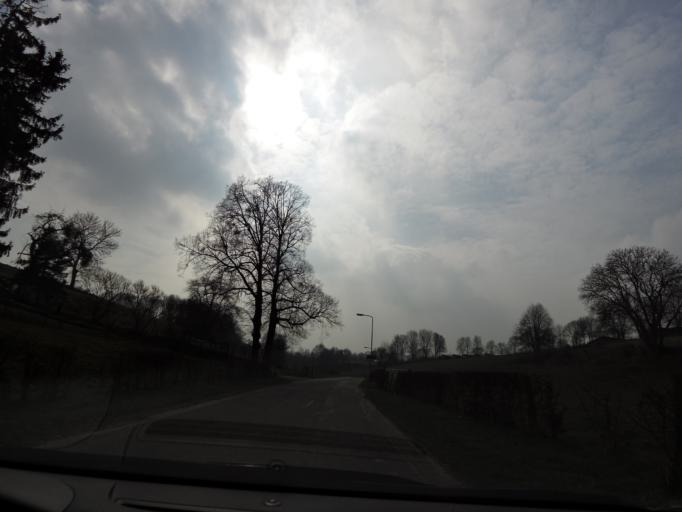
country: NL
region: Limburg
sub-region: Valkenburg aan de Geul
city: Schin op Geul
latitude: 50.8597
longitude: 5.8692
